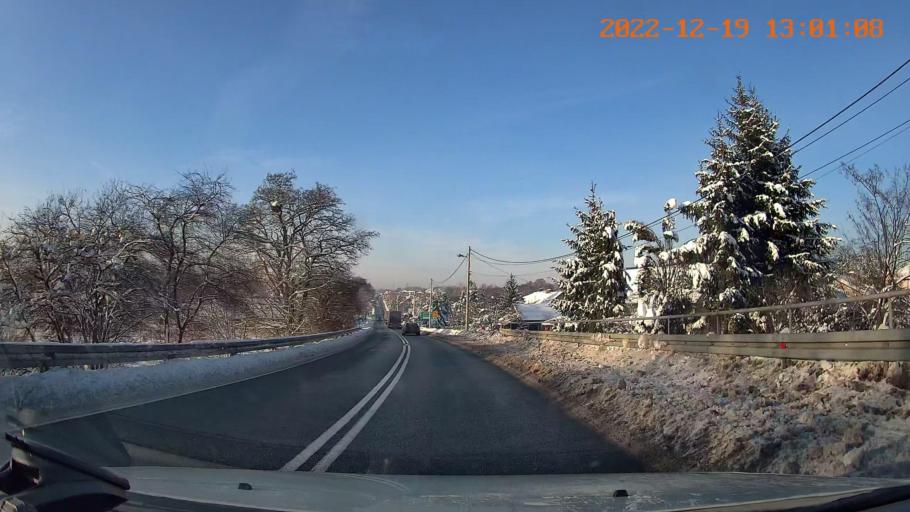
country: PL
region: Lesser Poland Voivodeship
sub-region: Powiat chrzanowski
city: Libiaz
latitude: 50.0886
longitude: 19.3078
